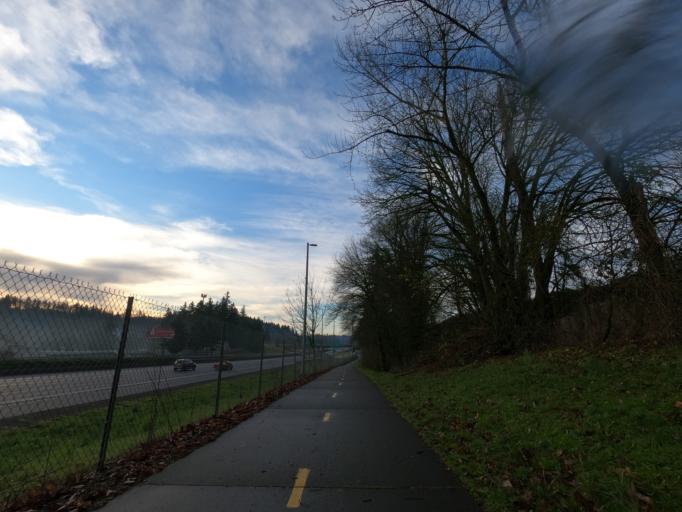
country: US
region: Oregon
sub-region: Clackamas County
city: Gladstone
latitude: 45.3885
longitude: -122.5782
